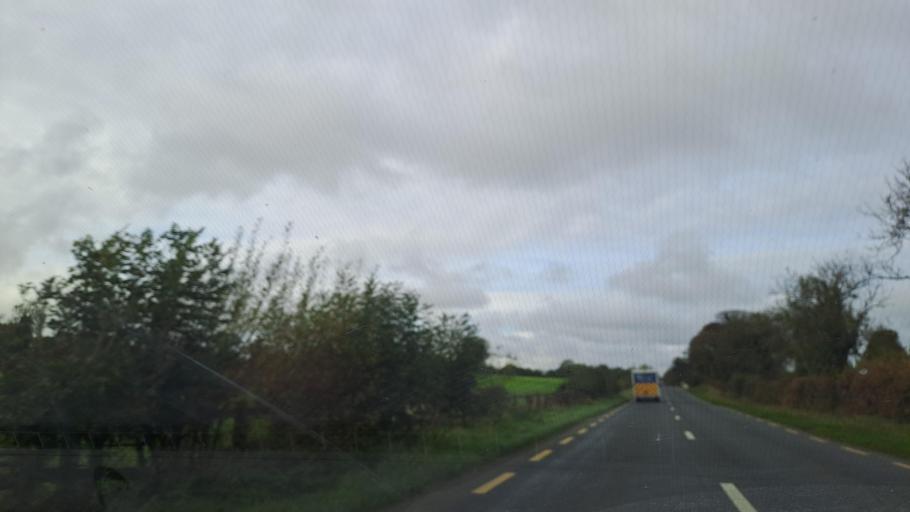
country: IE
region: Leinster
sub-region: An Mhi
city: Navan
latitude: 53.7612
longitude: -6.7249
